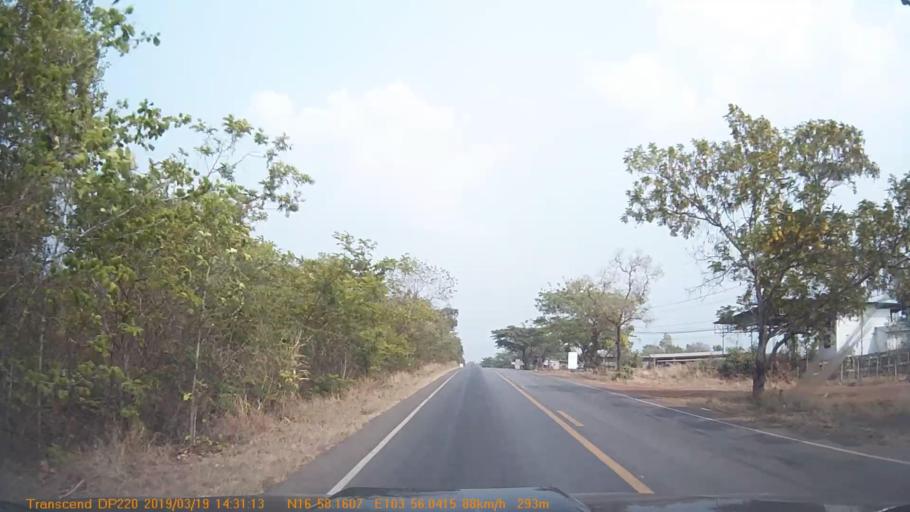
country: TH
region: Sakon Nakhon
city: Phu Phan
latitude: 16.9692
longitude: 103.9347
